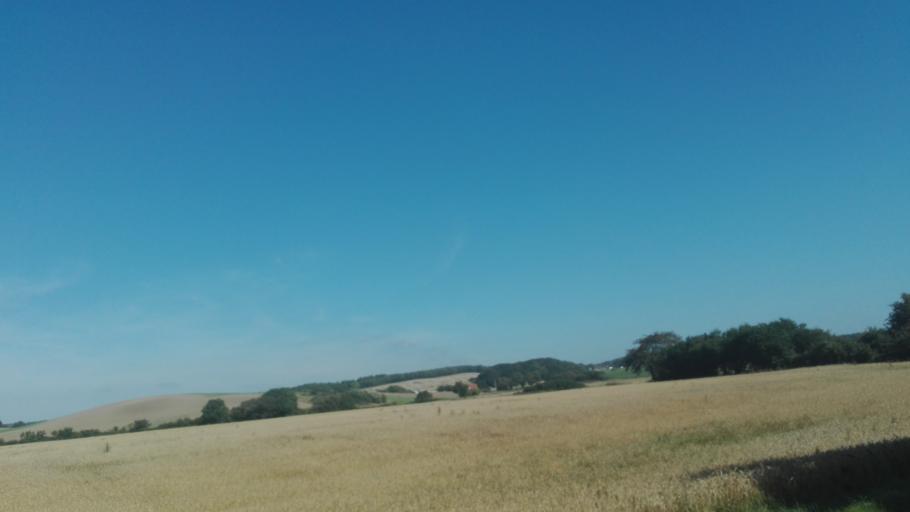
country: DK
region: Central Jutland
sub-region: Syddjurs Kommune
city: Ebeltoft
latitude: 56.2443
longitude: 10.7762
